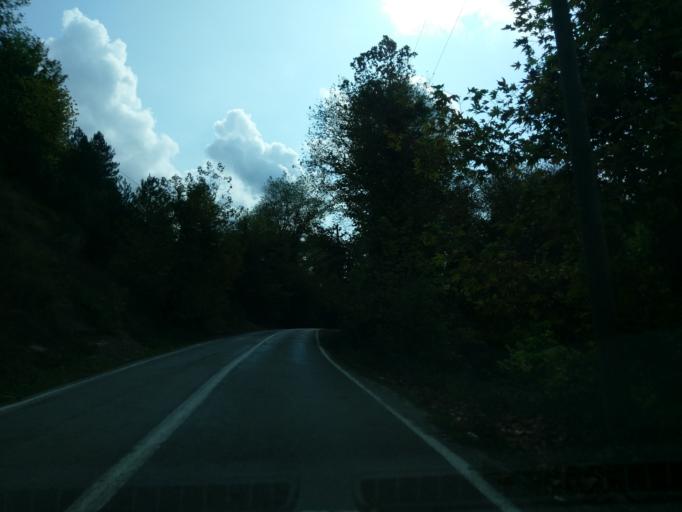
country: TR
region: Sinop
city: Helaldi
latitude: 41.9011
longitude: 34.4586
